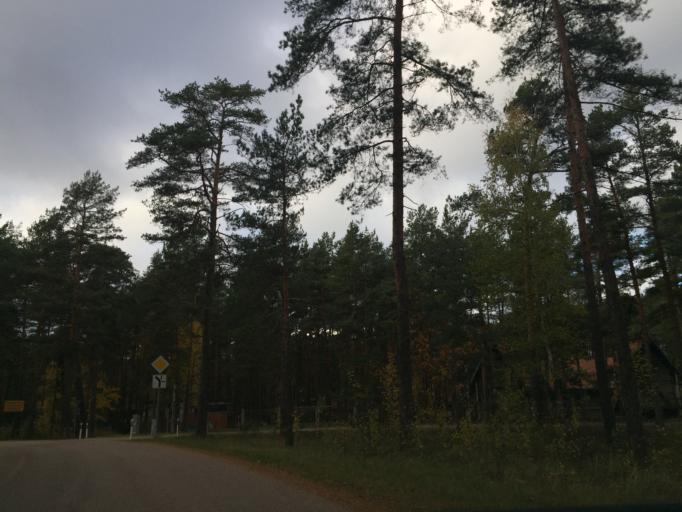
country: LV
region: Carnikava
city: Carnikava
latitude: 57.1419
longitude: 24.2960
